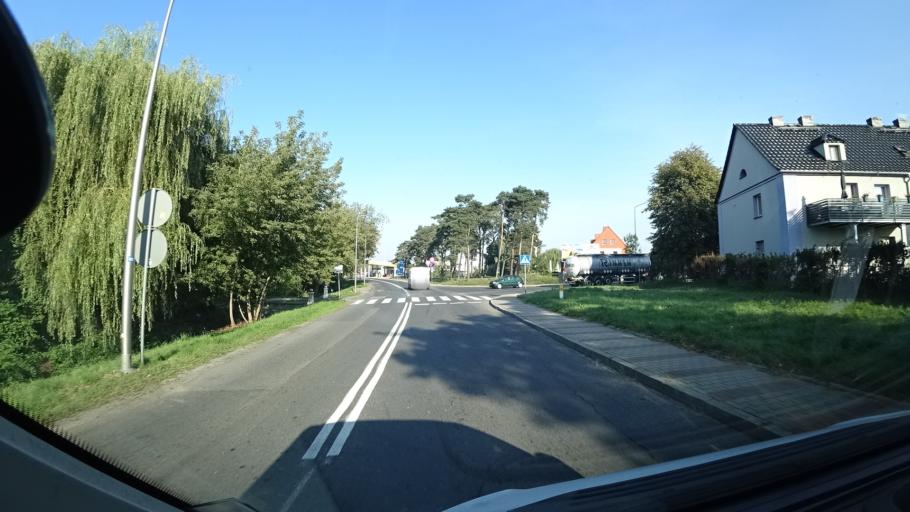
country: PL
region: Opole Voivodeship
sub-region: Powiat kedzierzynsko-kozielski
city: Kedzierzyn-Kozle
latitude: 50.3348
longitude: 18.1920
